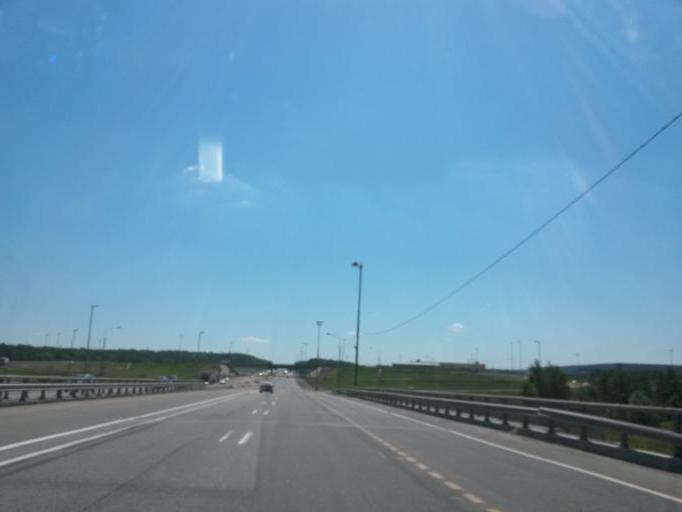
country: RU
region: Moskovskaya
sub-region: Chekhovskiy Rayon
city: Chekhov
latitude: 55.1349
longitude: 37.5627
